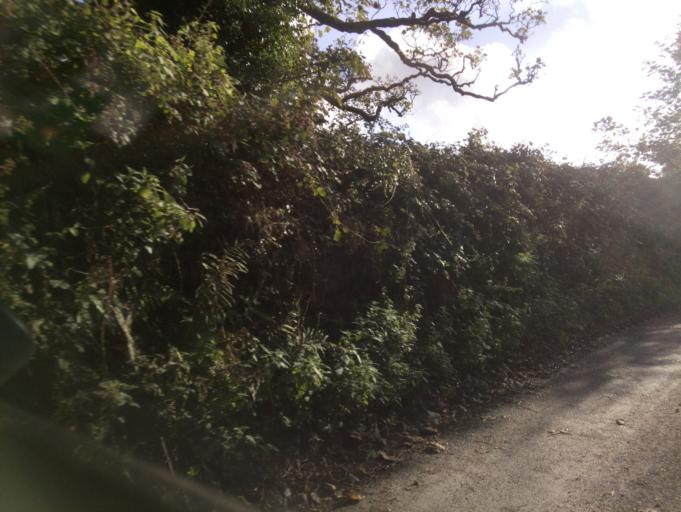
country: GB
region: England
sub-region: Devon
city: Dartmouth
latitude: 50.3461
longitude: -3.6602
